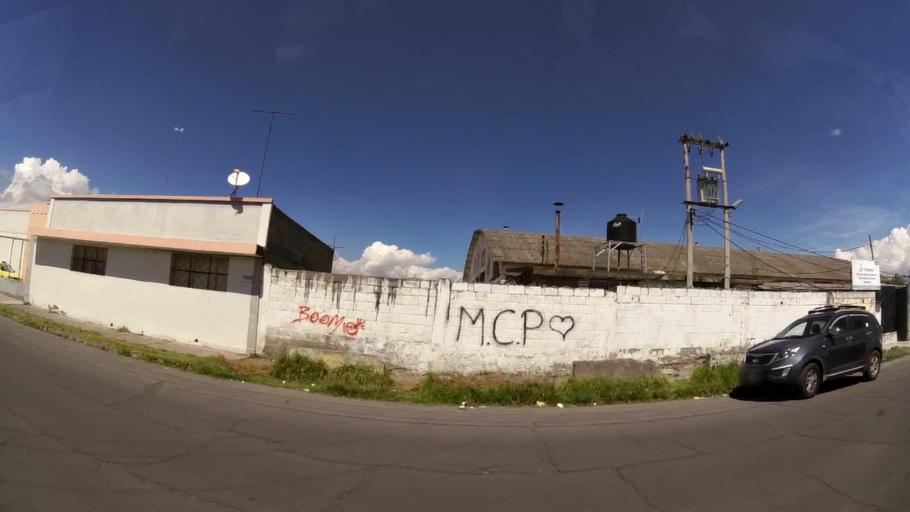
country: EC
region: Chimborazo
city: Riobamba
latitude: -1.6795
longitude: -78.6326
